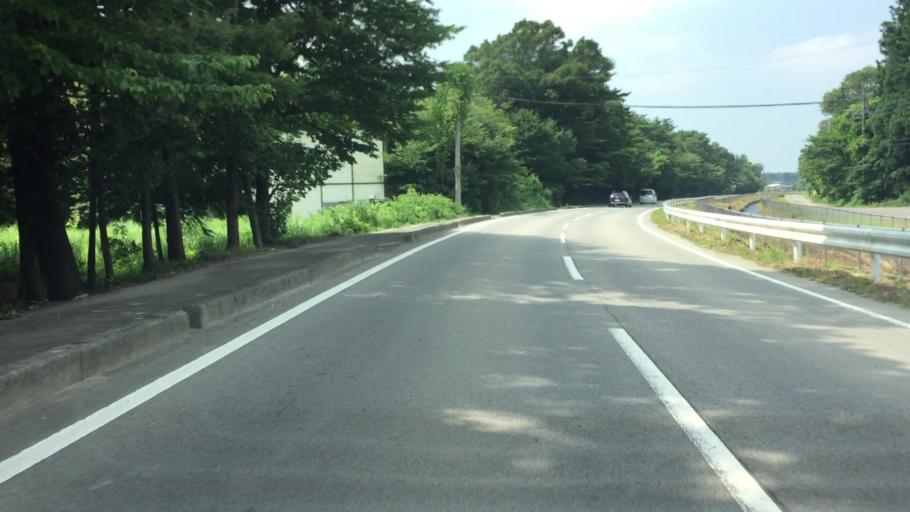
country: JP
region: Tochigi
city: Kuroiso
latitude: 37.0156
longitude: 140.0060
